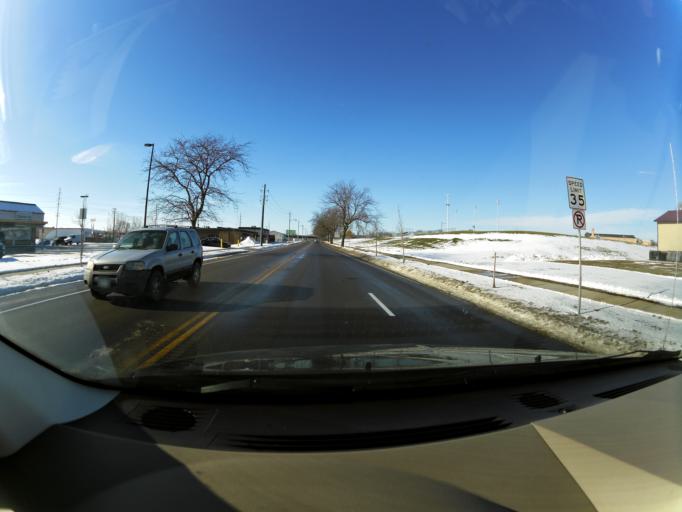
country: US
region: Minnesota
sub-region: Olmsted County
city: Rochester
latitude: 44.0318
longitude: -92.4817
